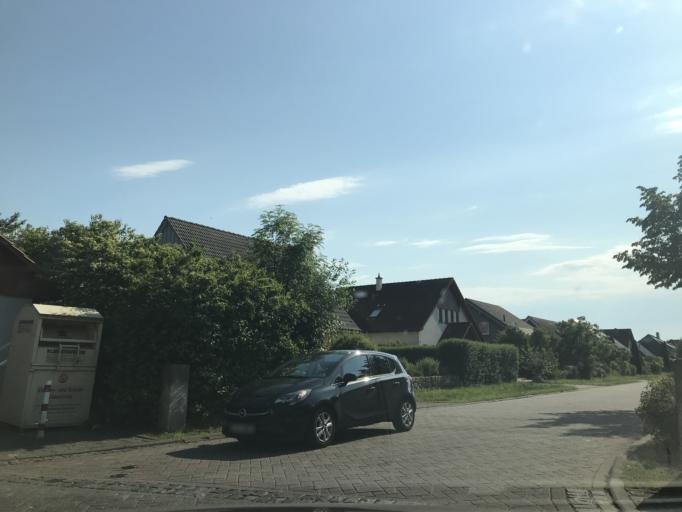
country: DE
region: Lower Saxony
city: Sehnde
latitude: 52.3405
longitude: 9.9351
